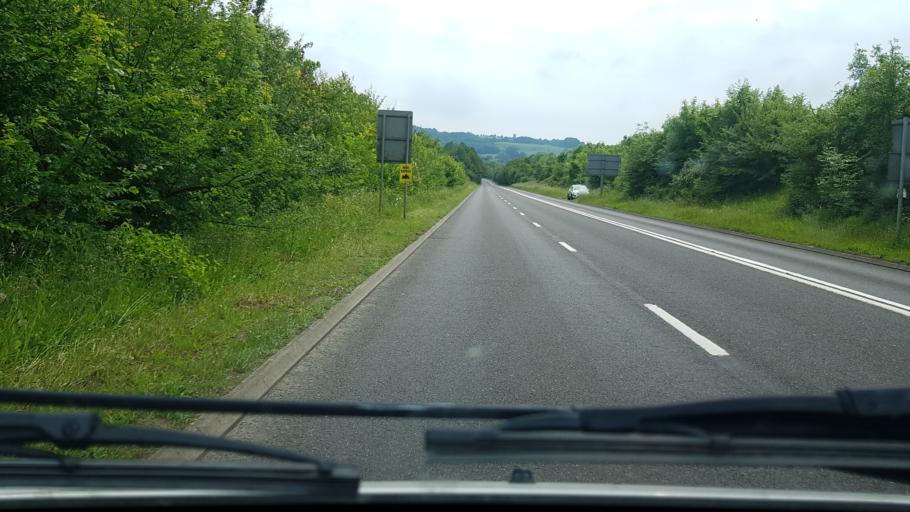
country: GB
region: England
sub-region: Worcestershire
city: Broadway
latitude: 52.0441
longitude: -1.8520
